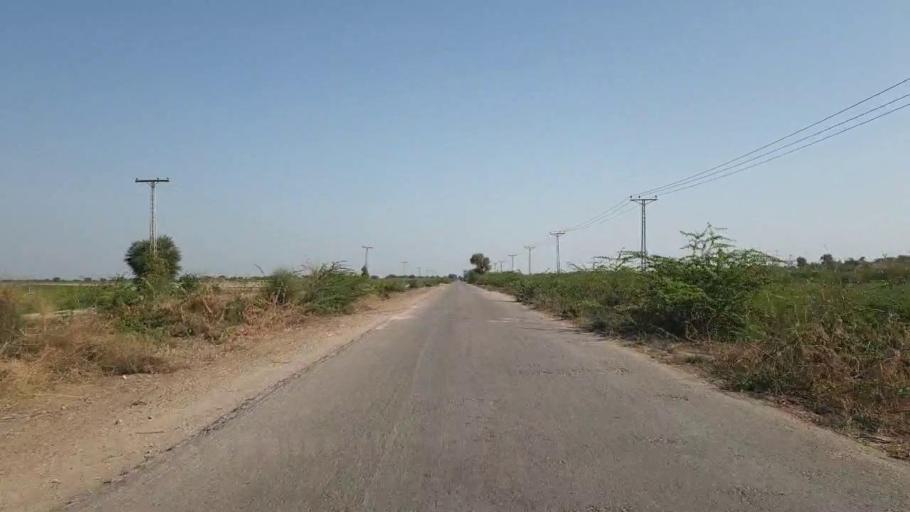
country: PK
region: Sindh
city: Umarkot
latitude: 25.4269
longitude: 69.7399
